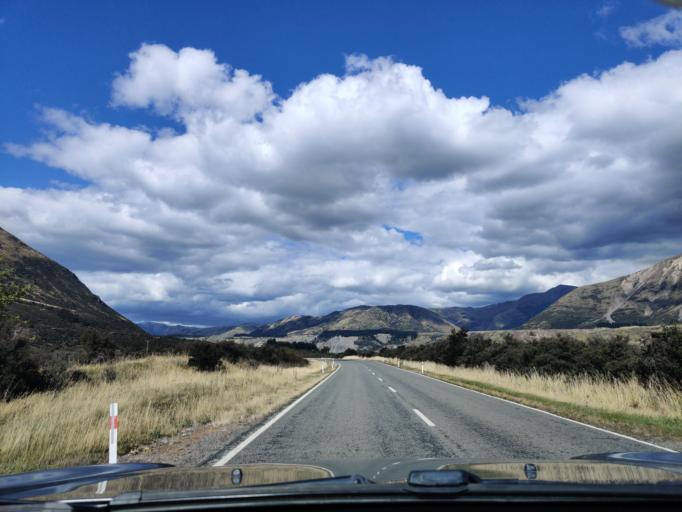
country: NZ
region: Canterbury
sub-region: Hurunui District
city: Amberley
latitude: -42.5858
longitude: 172.3882
